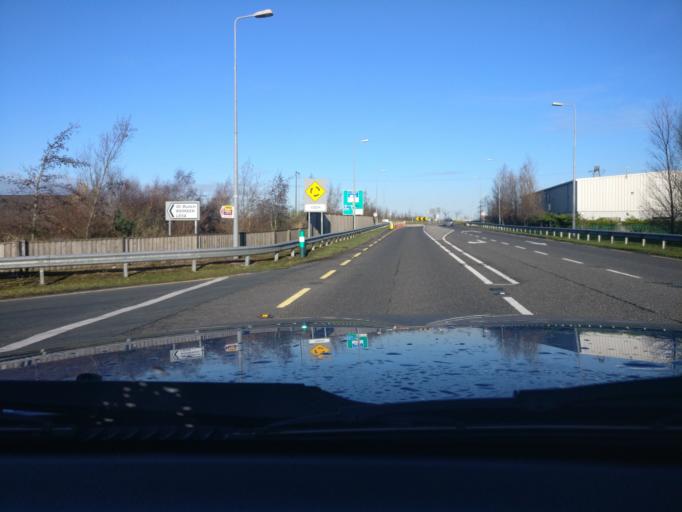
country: IE
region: Connaught
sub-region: County Galway
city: Loughrea
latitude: 53.2629
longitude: -8.6082
